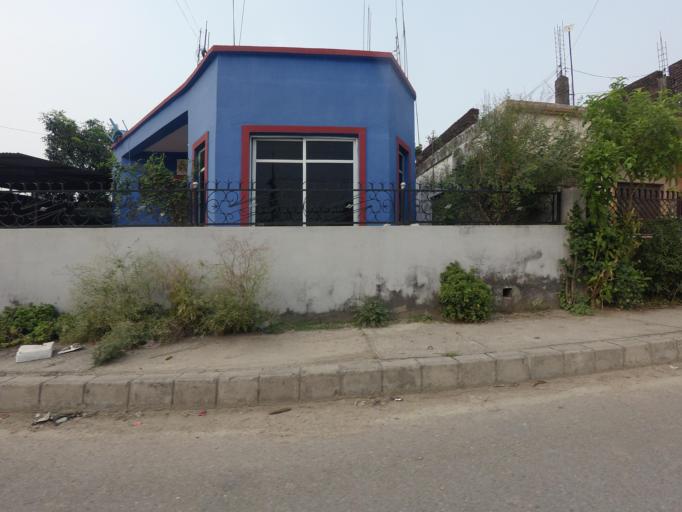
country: NP
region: Western Region
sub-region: Lumbini Zone
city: Bhairahawa
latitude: 27.5184
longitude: 83.4438
